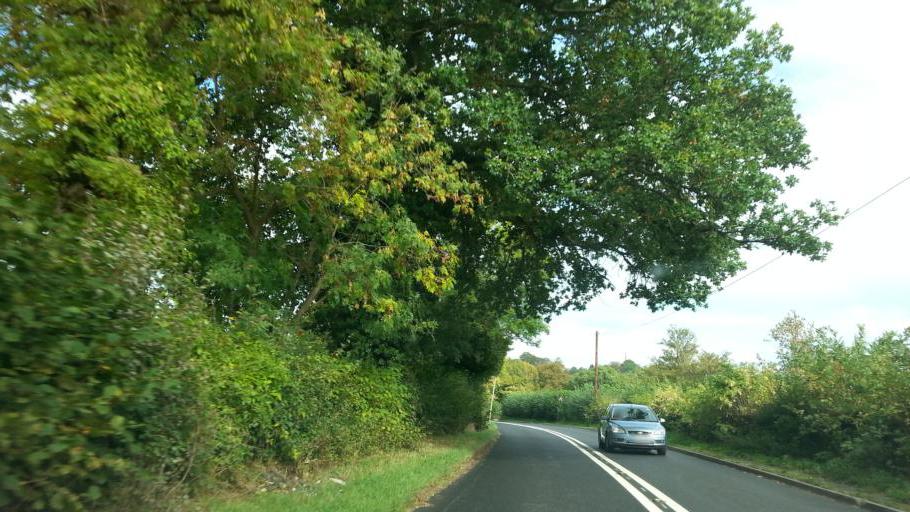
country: GB
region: England
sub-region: Gloucestershire
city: Painswick
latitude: 51.7776
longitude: -2.2073
